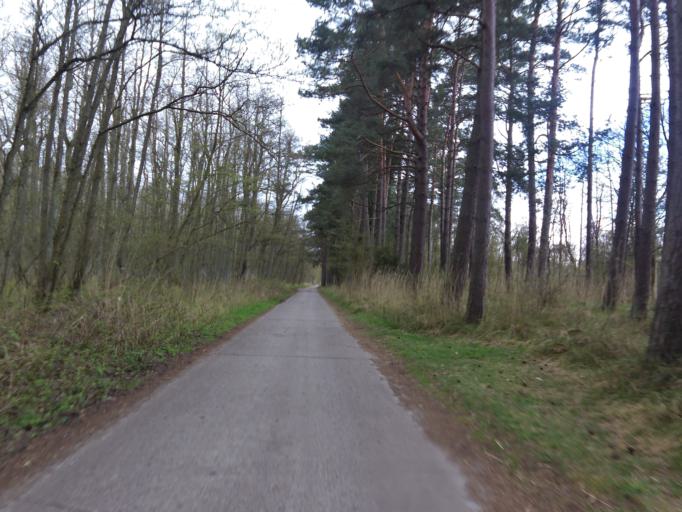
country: DE
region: Mecklenburg-Vorpommern
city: Ostseebad Prerow
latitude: 54.4644
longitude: 12.5262
